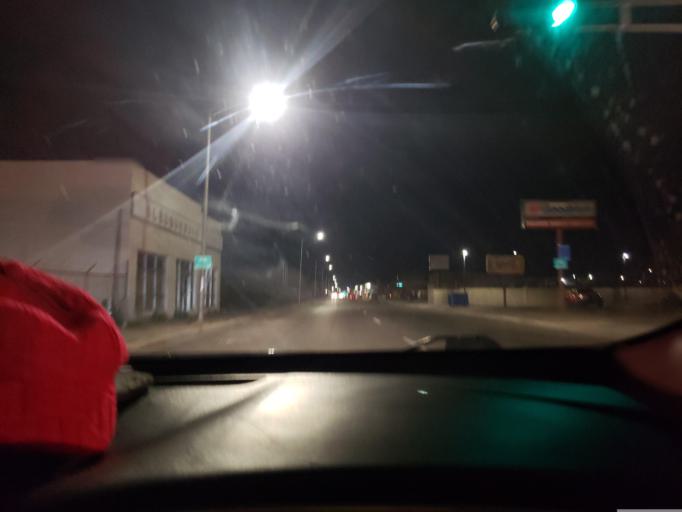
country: US
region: New Mexico
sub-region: Bernalillo County
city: Albuquerque
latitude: 35.0948
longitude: -106.6474
